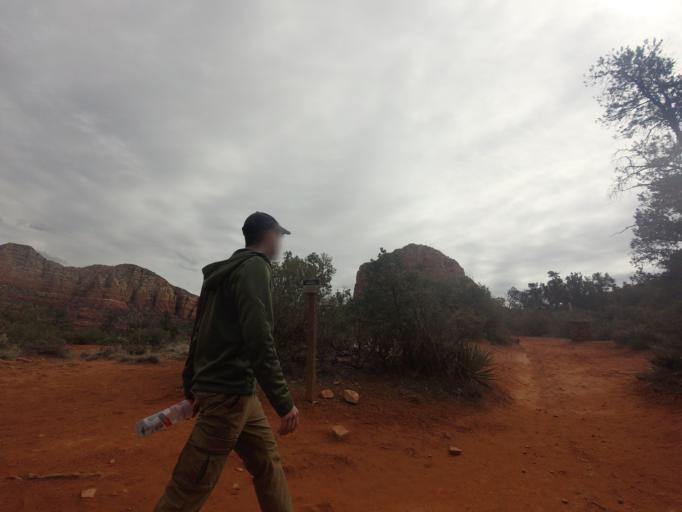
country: US
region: Arizona
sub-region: Yavapai County
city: Village of Oak Creek (Big Park)
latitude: 34.8034
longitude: -111.7659
